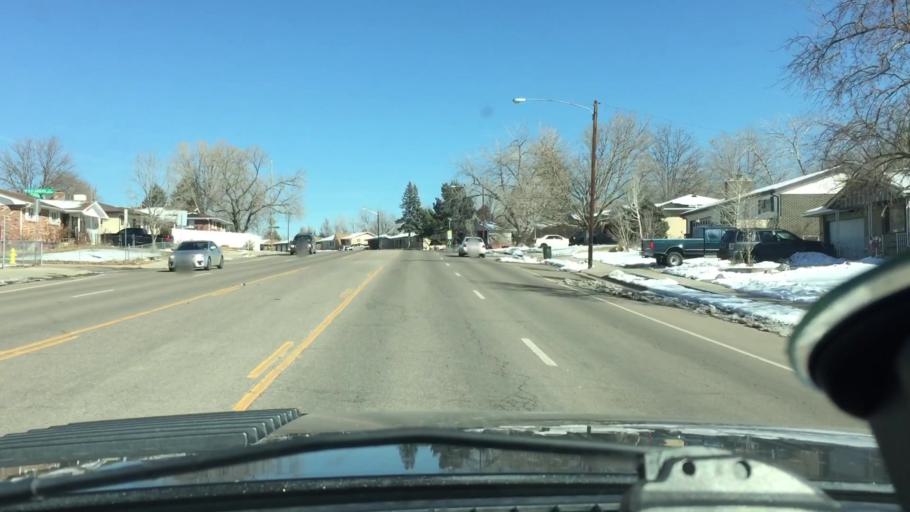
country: US
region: Colorado
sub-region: Adams County
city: Sherrelwood
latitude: 39.8420
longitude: -105.0006
